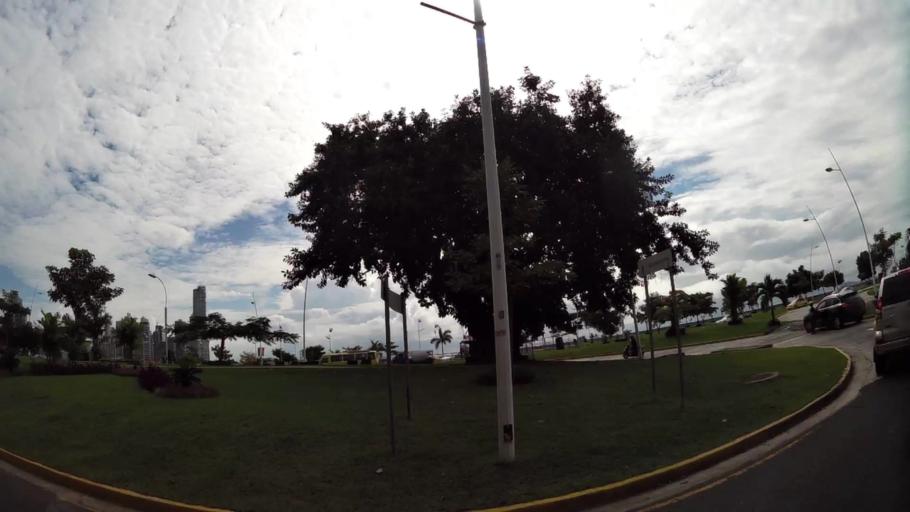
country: PA
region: Panama
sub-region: Distrito de Panama
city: Ancon
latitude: 8.9700
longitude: -79.5306
